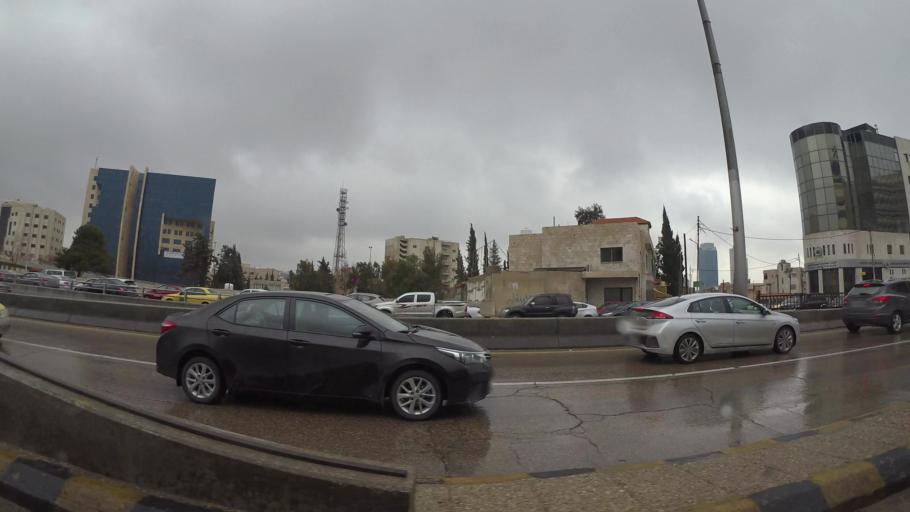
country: JO
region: Amman
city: Amman
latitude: 31.9715
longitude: 35.9080
